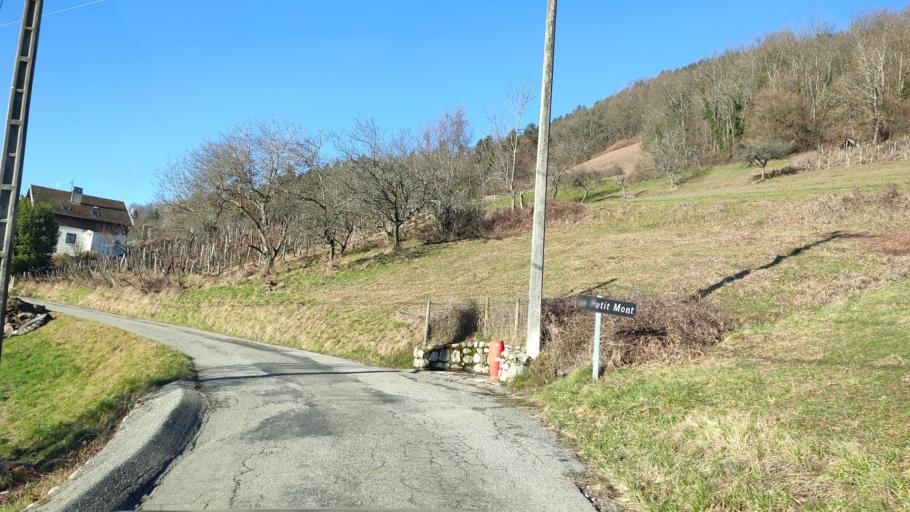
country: FR
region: Rhone-Alpes
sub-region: Departement de la Savoie
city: La Rochette
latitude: 45.4626
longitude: 6.1067
